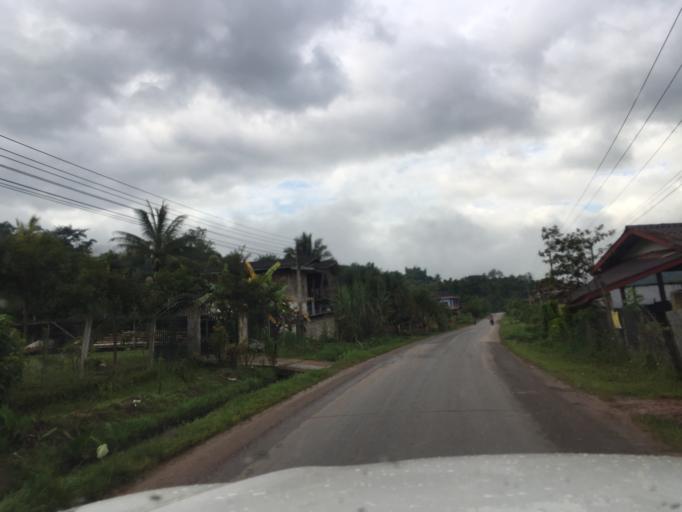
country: LA
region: Oudomxai
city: Muang La
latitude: 20.8545
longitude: 102.1099
